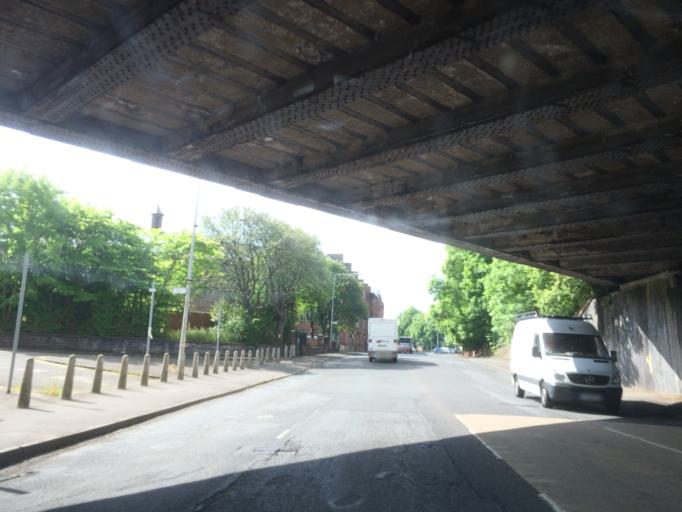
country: GB
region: Scotland
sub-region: East Renfrewshire
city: Giffnock
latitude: 55.8292
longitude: -4.2957
